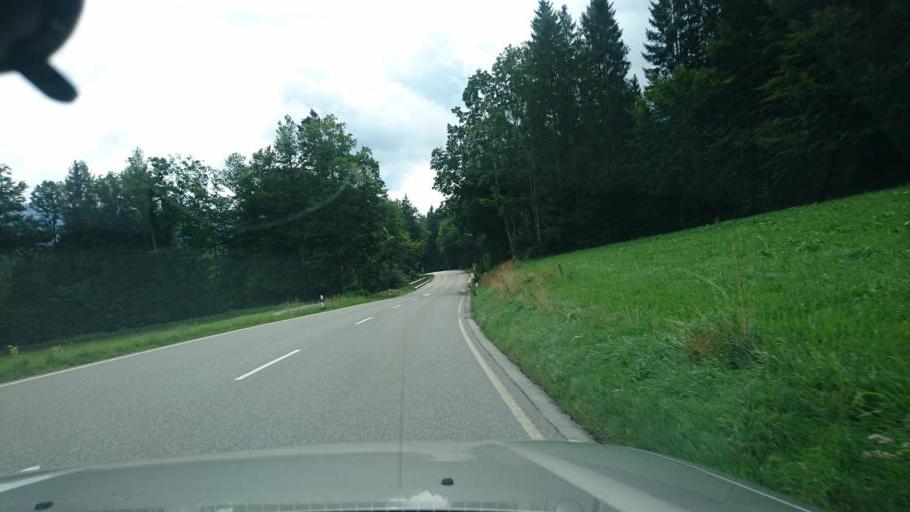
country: DE
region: Bavaria
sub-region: Upper Bavaria
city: Inzell
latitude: 47.7522
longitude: 12.7181
